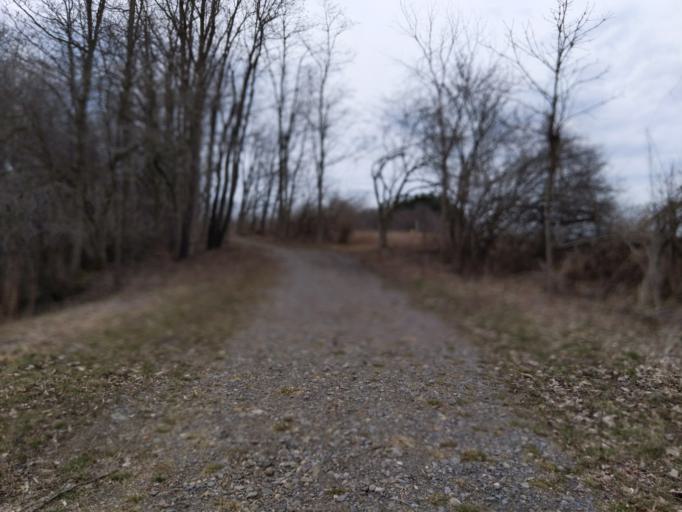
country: US
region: New York
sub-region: Tompkins County
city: Dryden
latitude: 42.4975
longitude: -76.3267
